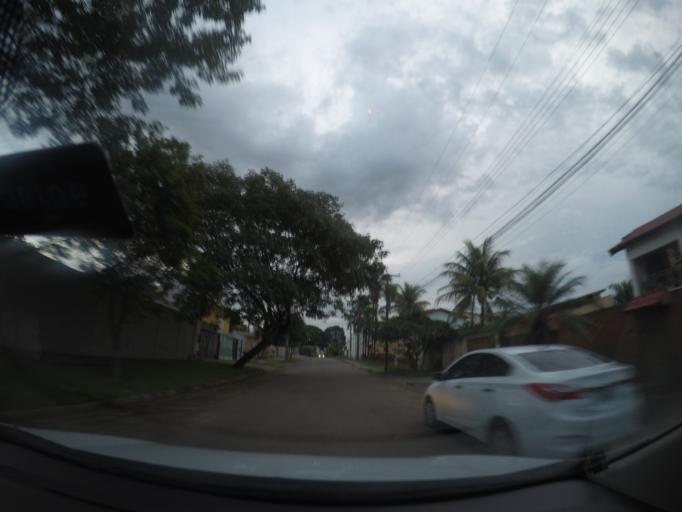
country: BR
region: Goias
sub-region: Goiania
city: Goiania
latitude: -16.6465
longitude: -49.2303
